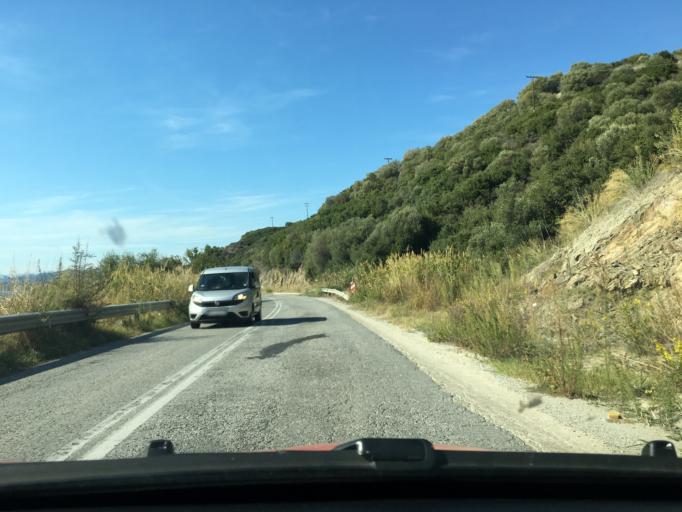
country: GR
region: Central Macedonia
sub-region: Nomos Chalkidikis
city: Nea Roda
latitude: 40.3557
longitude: 23.9450
